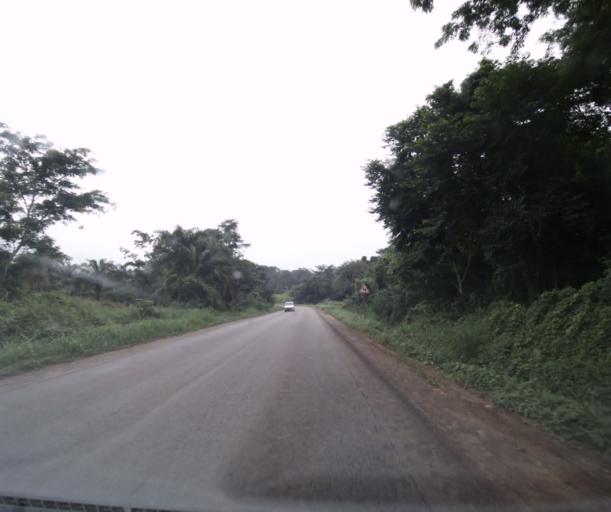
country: CM
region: Littoral
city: Edea
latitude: 3.8451
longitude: 10.4726
